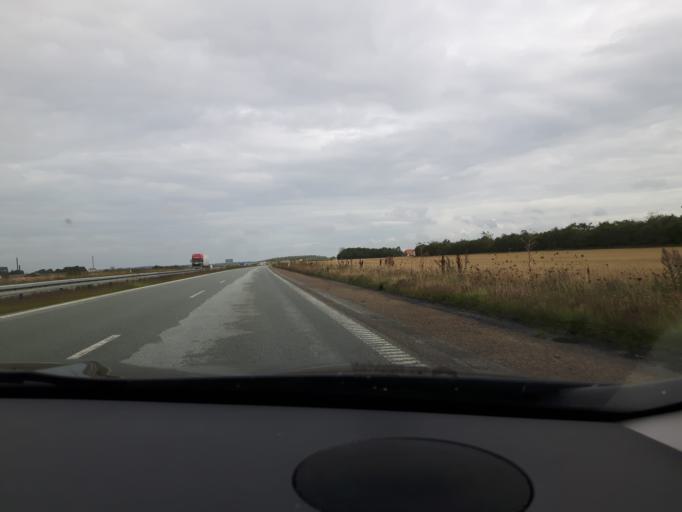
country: DK
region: North Denmark
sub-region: Hjorring Kommune
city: Hjorring
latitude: 57.4332
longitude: 10.0340
